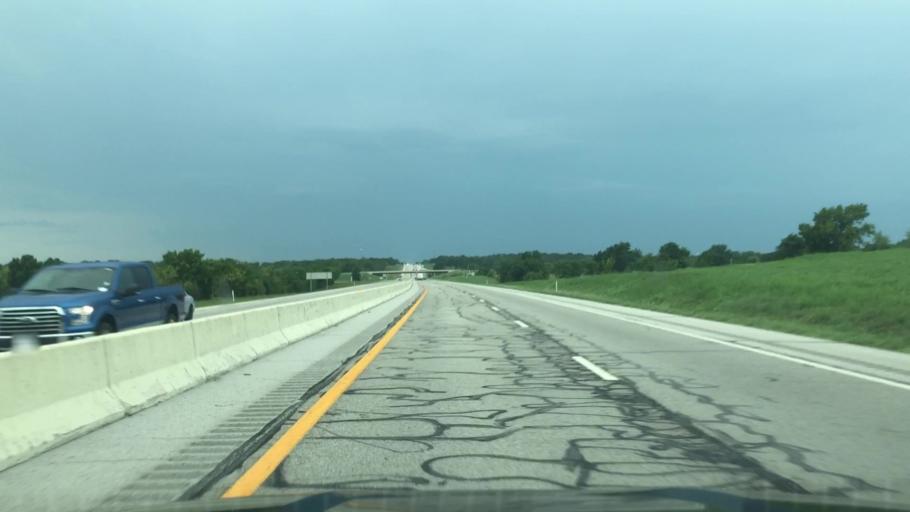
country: US
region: Oklahoma
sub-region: Rogers County
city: Chelsea
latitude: 36.4435
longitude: -95.3762
